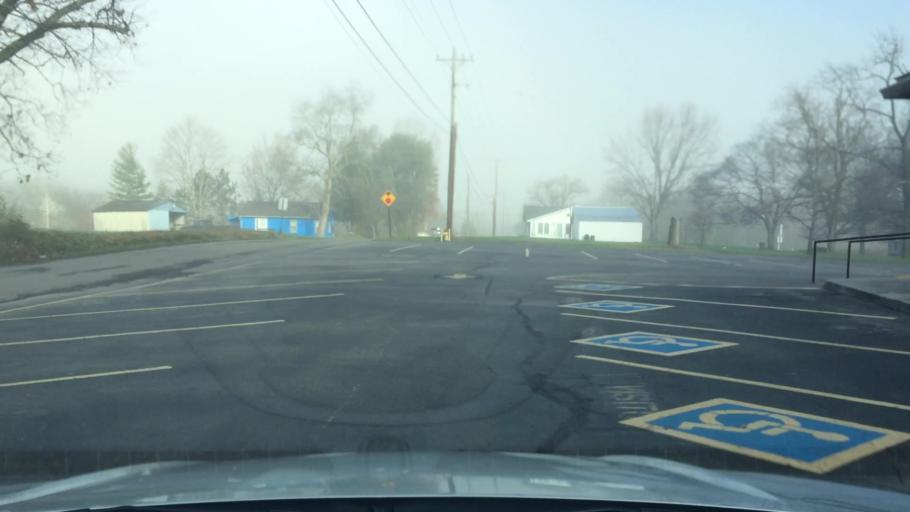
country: US
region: Tennessee
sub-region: Blount County
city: Maryville
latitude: 35.7281
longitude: -84.0324
